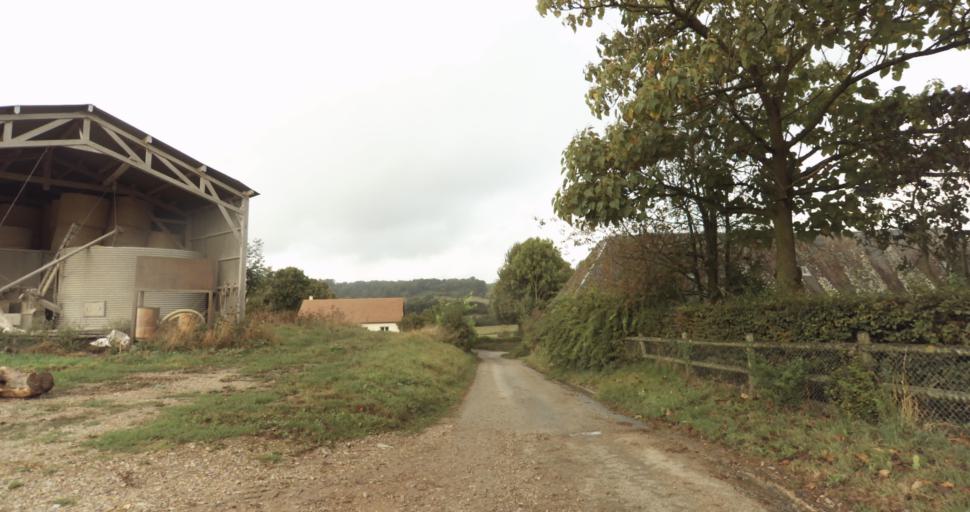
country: FR
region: Lower Normandy
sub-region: Departement de l'Orne
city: Gace
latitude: 48.8833
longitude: 0.2842
